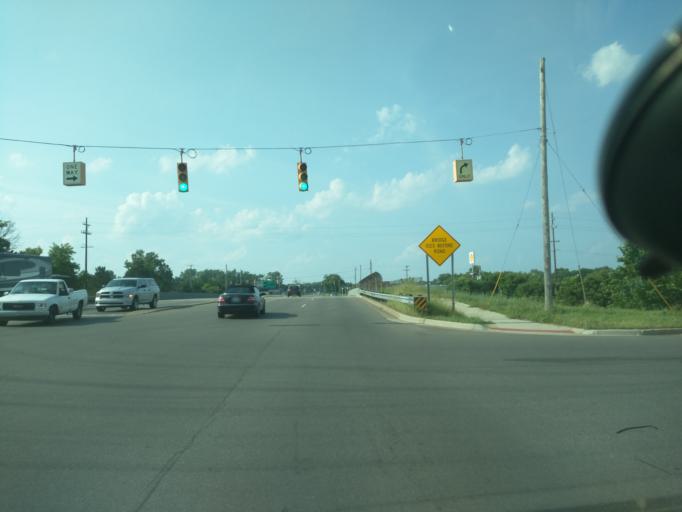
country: US
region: Michigan
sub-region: Jackson County
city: Jackson
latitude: 42.2682
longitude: -84.4528
